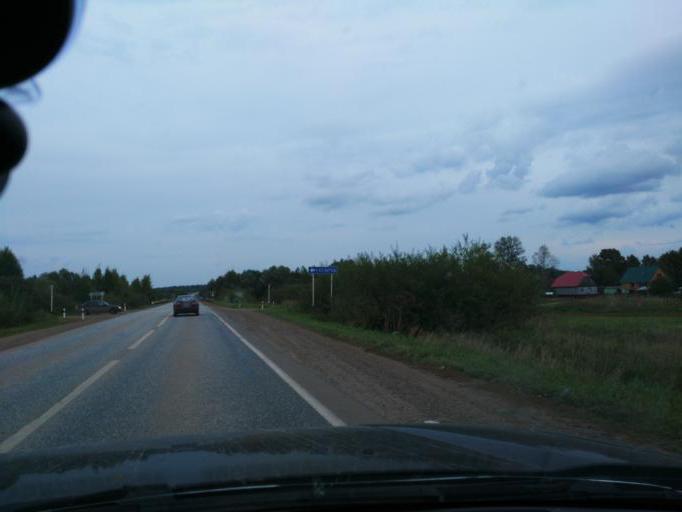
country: RU
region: Perm
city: Chernushka
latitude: 56.5135
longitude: 56.0104
